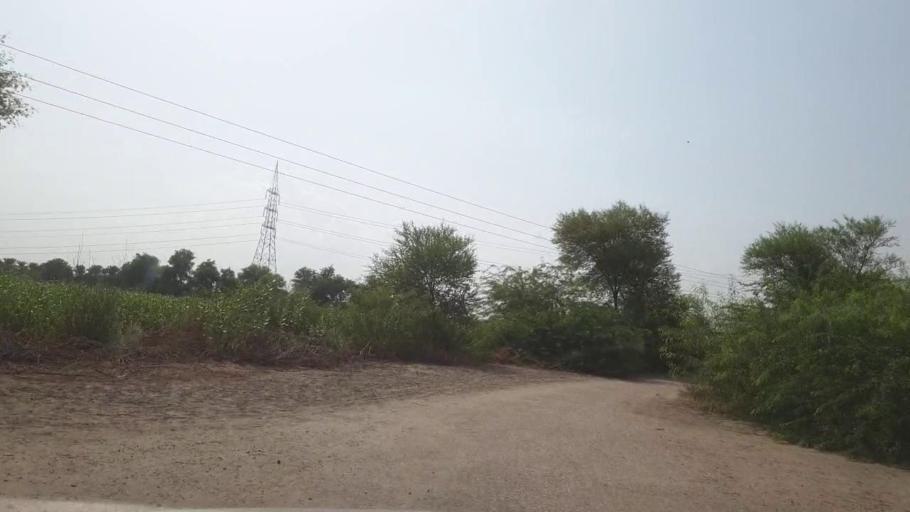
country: PK
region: Sindh
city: Pano Aqil
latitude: 27.7678
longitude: 69.1688
